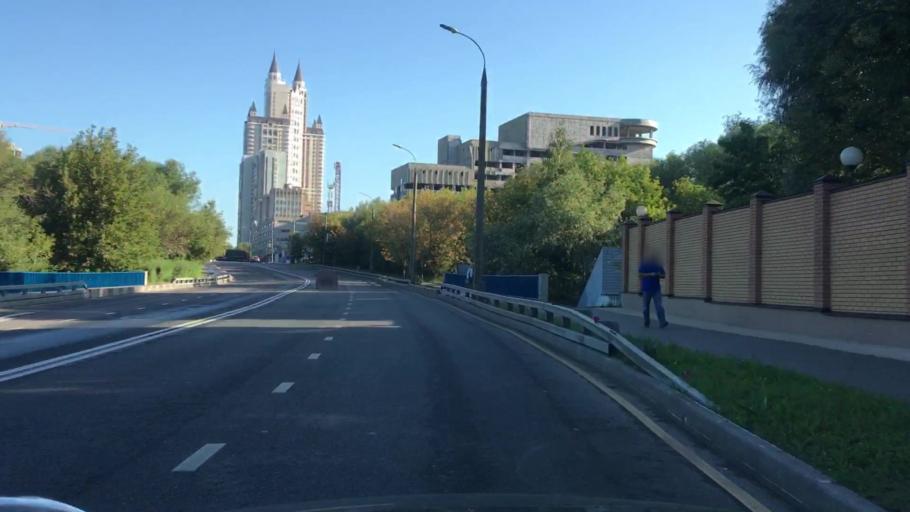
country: RU
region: Moscow
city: Davydkovo
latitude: 55.7207
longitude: 37.4784
